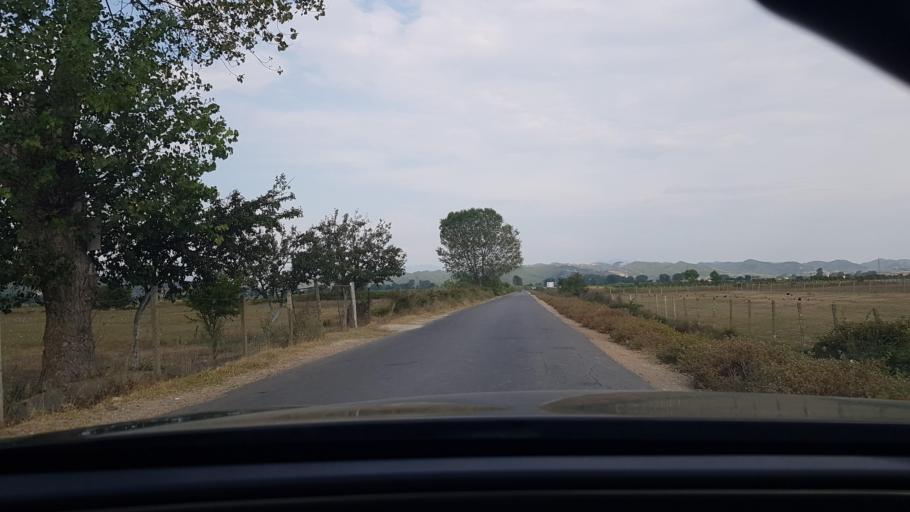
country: AL
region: Durres
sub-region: Rrethi i Durresit
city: Katundi i Ri
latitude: 41.4844
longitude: 19.5296
